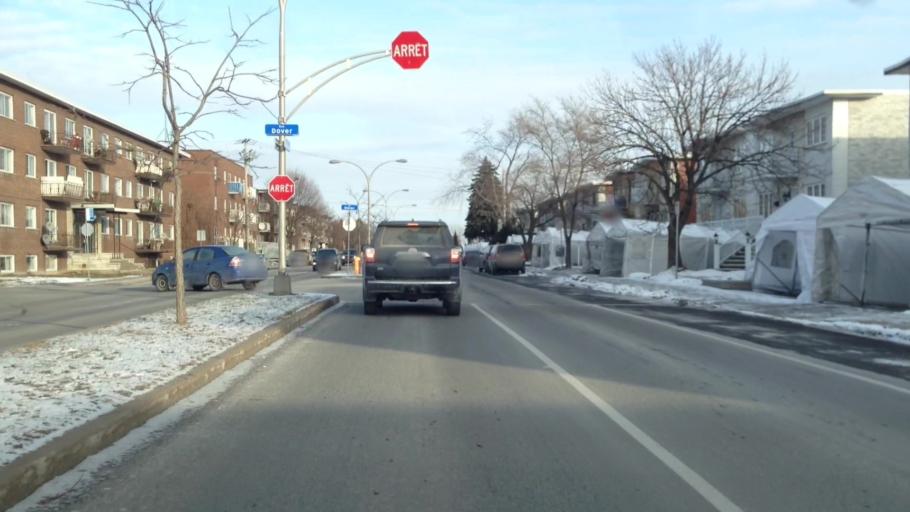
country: CA
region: Quebec
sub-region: Laval
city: Laval
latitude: 45.5381
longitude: -73.7562
